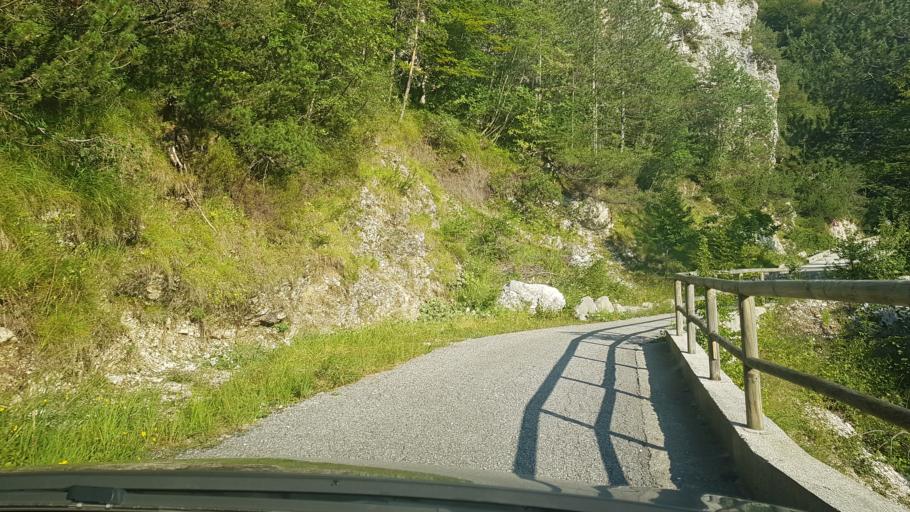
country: IT
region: Friuli Venezia Giulia
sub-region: Provincia di Udine
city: Moggio Udinese
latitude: 46.4502
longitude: 13.2169
